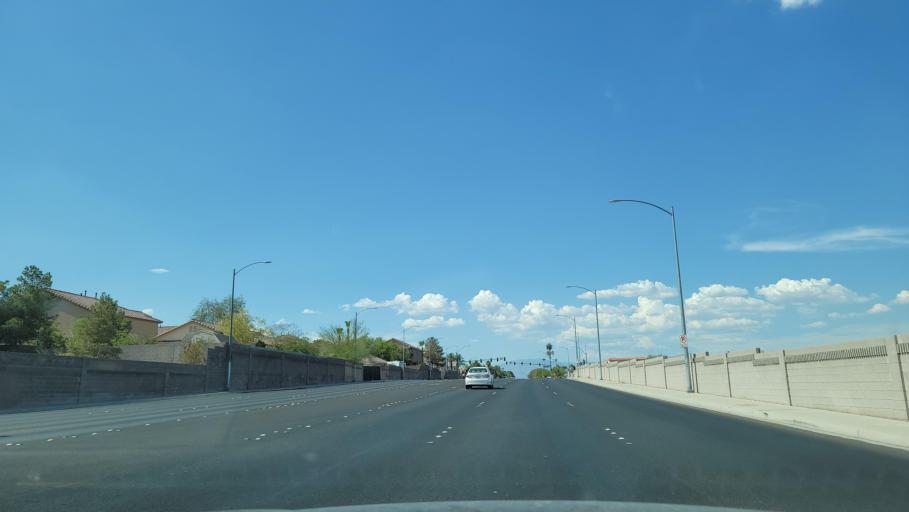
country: US
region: Nevada
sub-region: Clark County
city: Spring Valley
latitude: 36.1268
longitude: -115.2609
